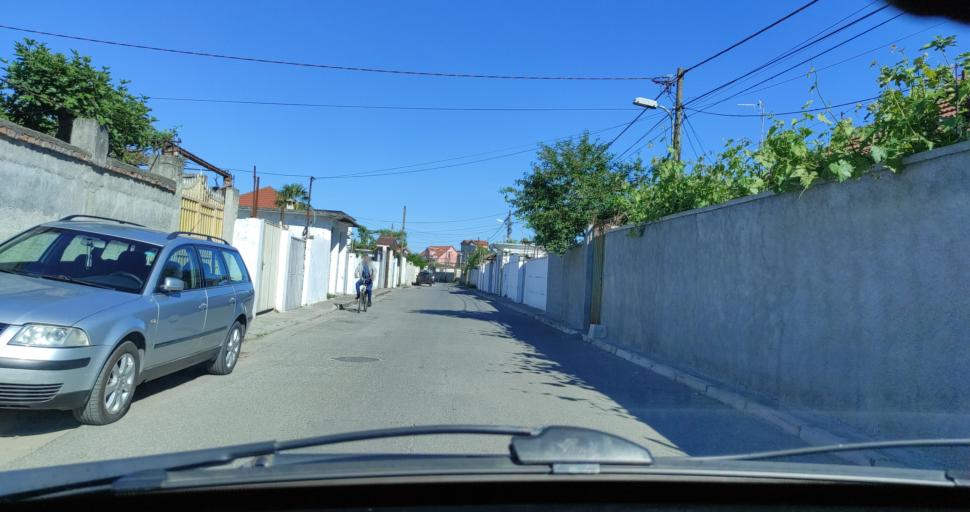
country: AL
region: Shkoder
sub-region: Rrethi i Shkodres
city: Shkoder
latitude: 42.0786
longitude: 19.5041
